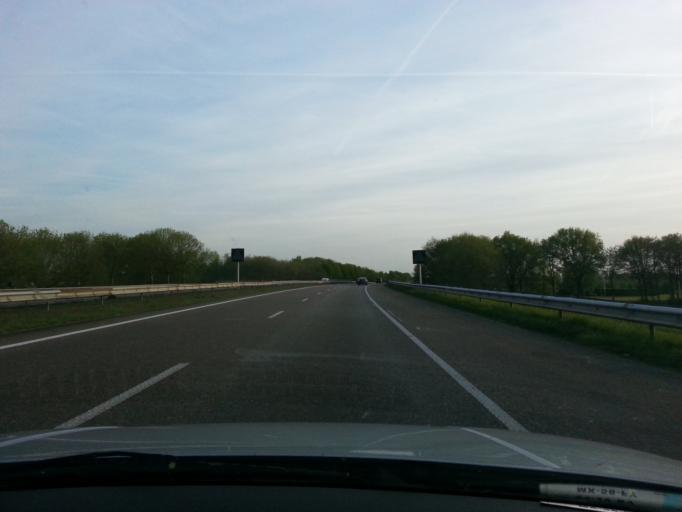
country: NL
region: Friesland
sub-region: Gemeente Opsterland
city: Tijnje
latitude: 52.9975
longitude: 5.9912
